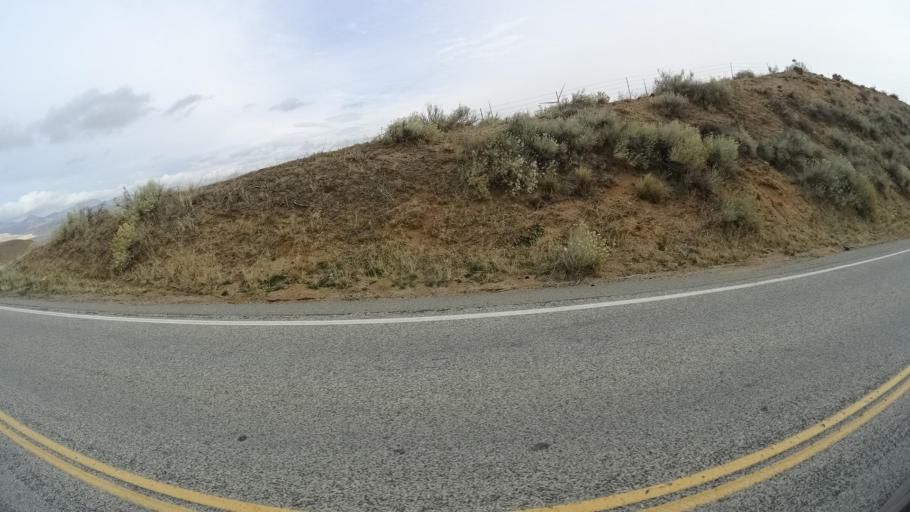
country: US
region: California
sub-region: Kern County
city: Tehachapi
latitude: 35.0885
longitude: -118.3962
